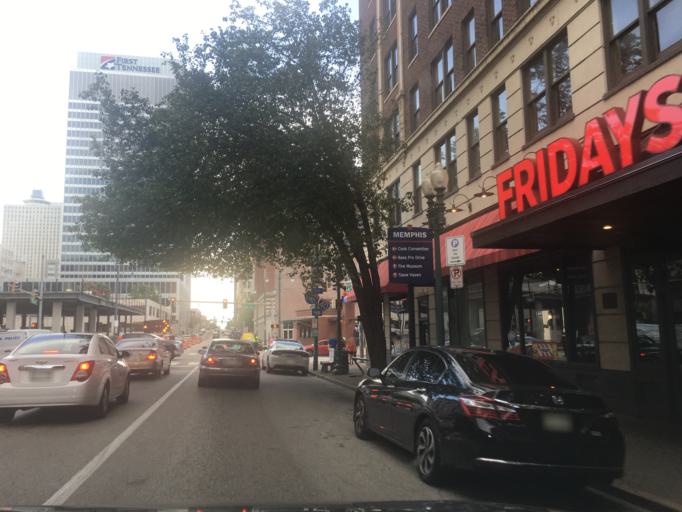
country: US
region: Tennessee
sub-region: Shelby County
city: Memphis
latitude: 35.1420
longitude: -90.0513
